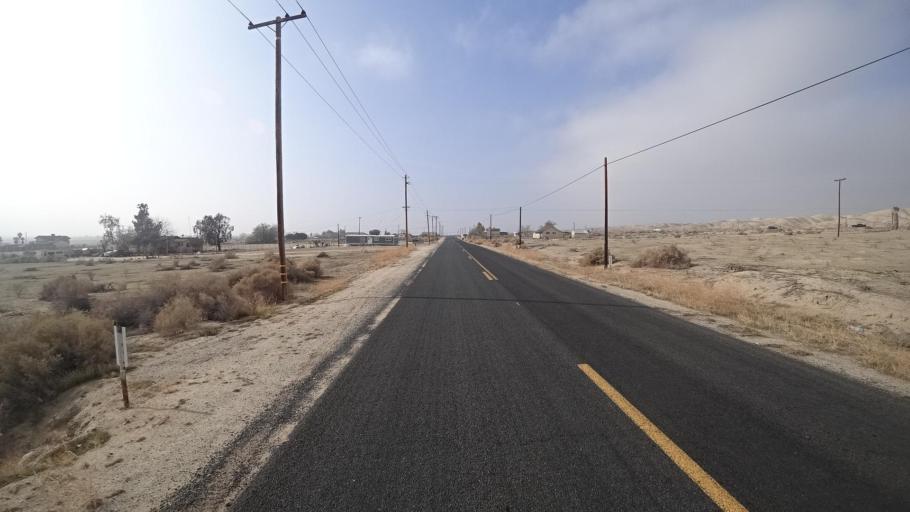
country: US
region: California
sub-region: Kern County
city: Ford City
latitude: 35.2322
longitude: -119.3670
